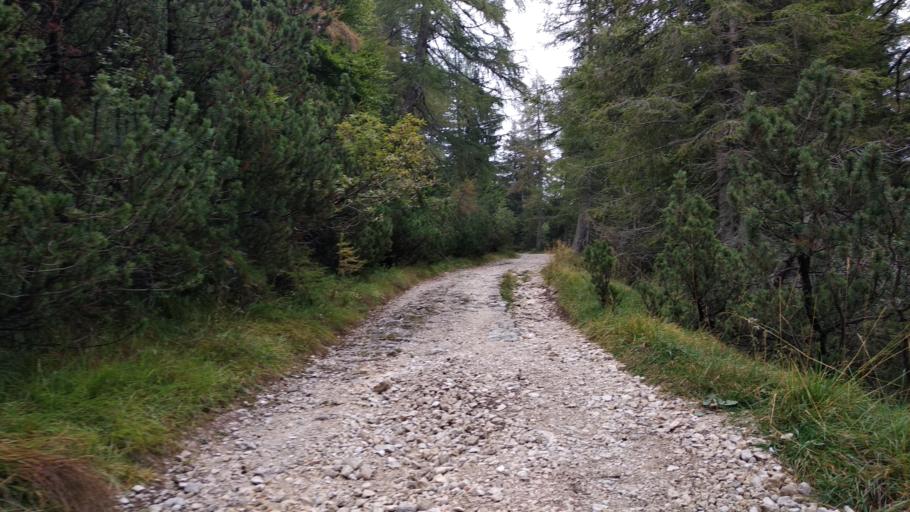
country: IT
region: Veneto
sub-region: Provincia di Vicenza
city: Roana
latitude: 45.9627
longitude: 11.4414
